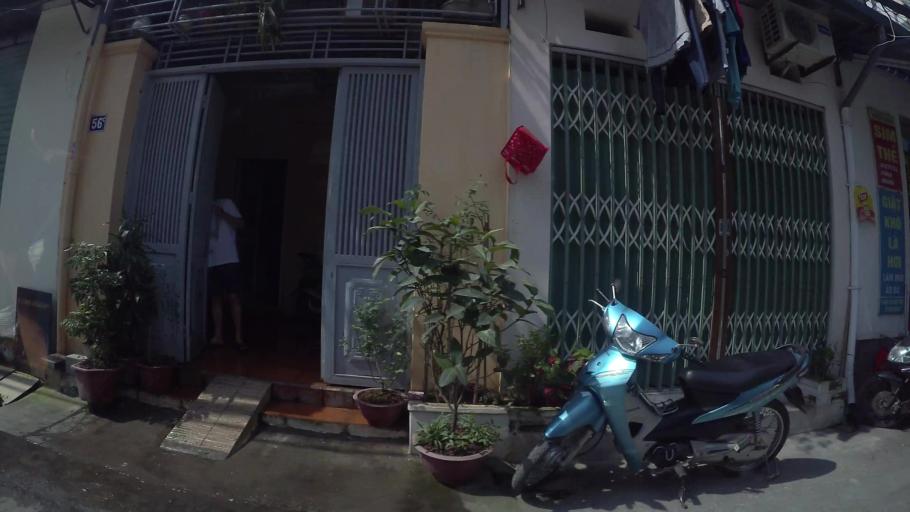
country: VN
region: Ha Noi
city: Hoan Kiem
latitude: 21.0514
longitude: 105.8662
